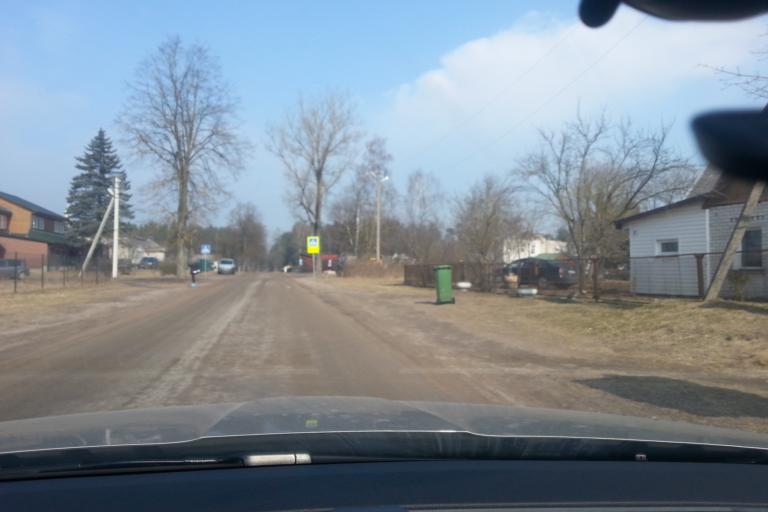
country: LT
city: Trakai
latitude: 54.5022
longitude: 24.9846
